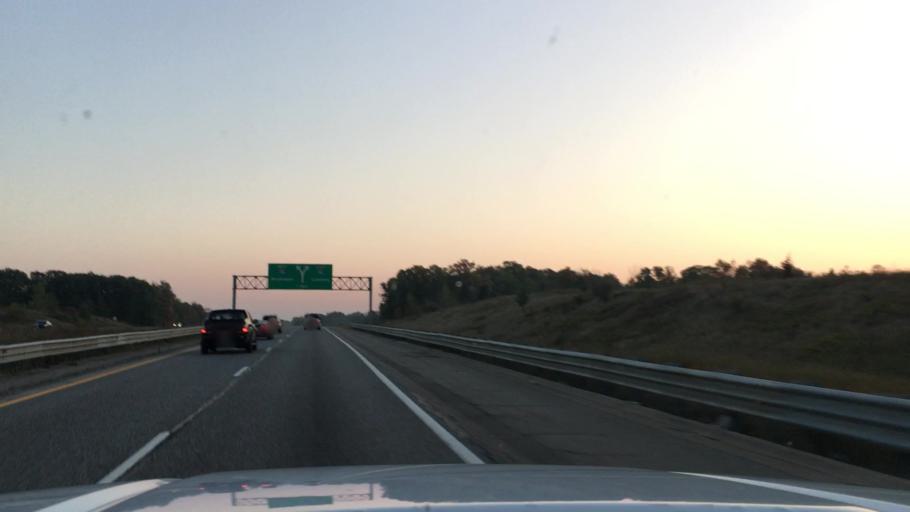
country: US
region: Michigan
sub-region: Kent County
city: Caledonia
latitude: 42.8661
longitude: -85.4978
